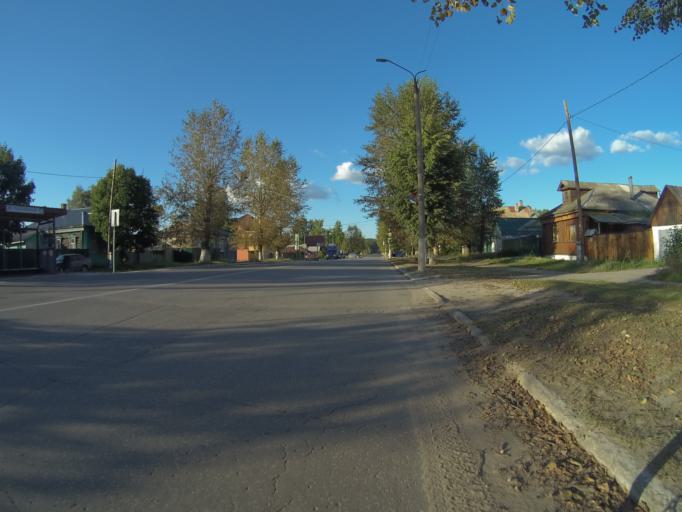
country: RU
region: Vladimir
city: Gus'-Khrustal'nyy
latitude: 55.6228
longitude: 40.6811
